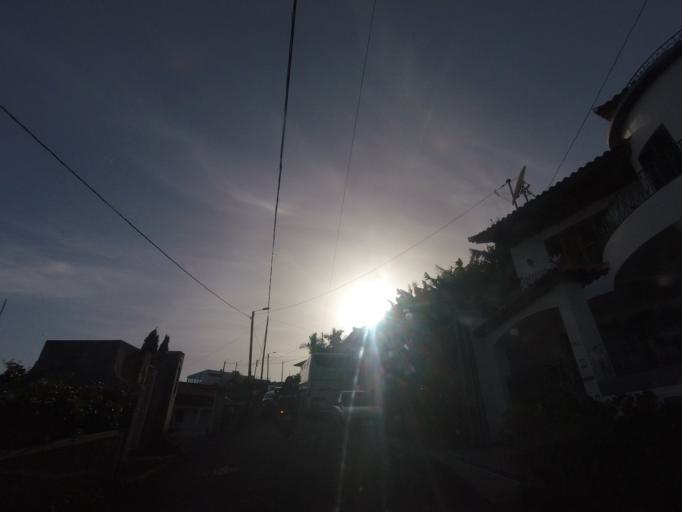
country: PT
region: Madeira
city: Camara de Lobos
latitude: 32.6532
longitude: -16.9916
